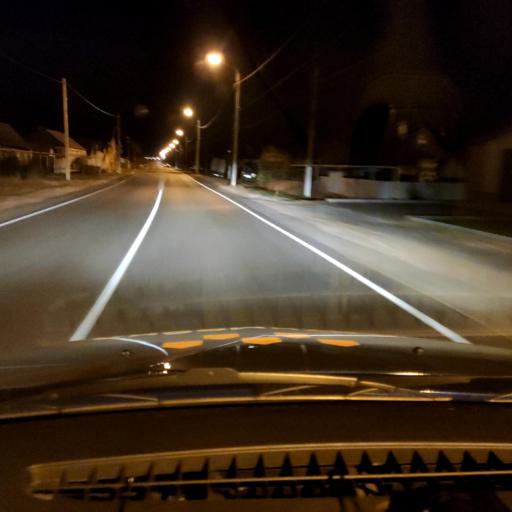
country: RU
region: Voronezj
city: Shilovo
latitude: 51.5776
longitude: 39.0376
